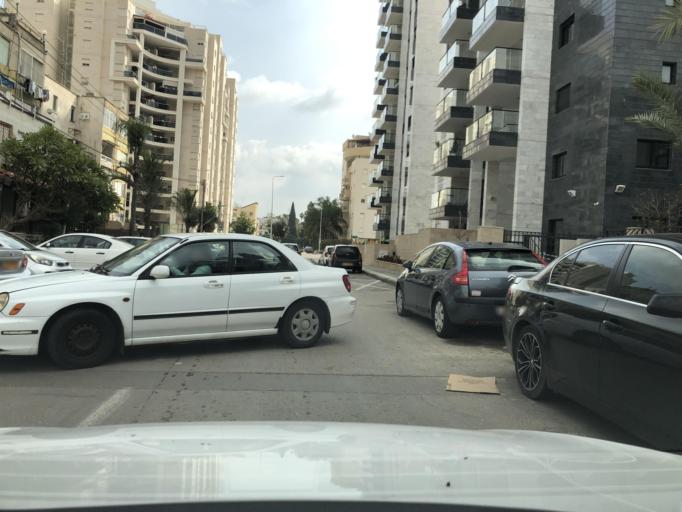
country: IL
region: Central District
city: Yehud
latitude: 32.0324
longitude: 34.8902
